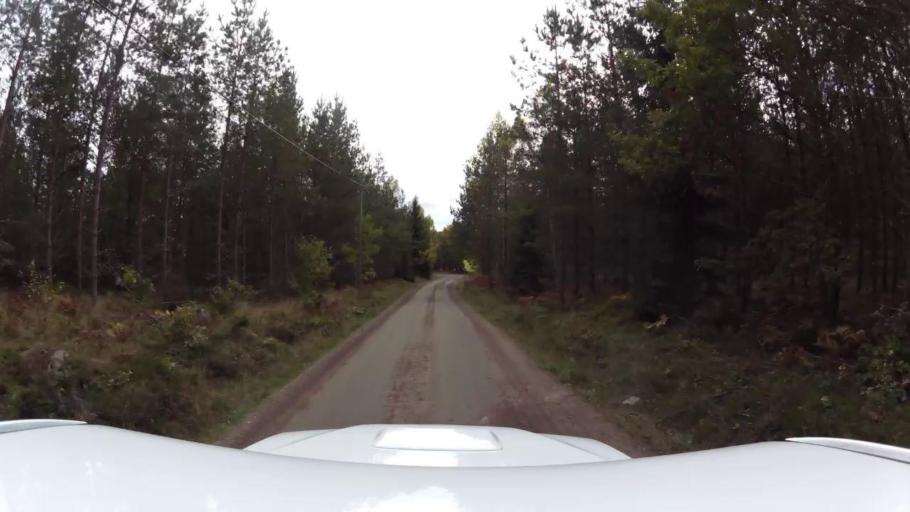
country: SE
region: OEstergoetland
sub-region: Linkopings Kommun
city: Ekangen
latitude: 58.5506
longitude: 15.6627
